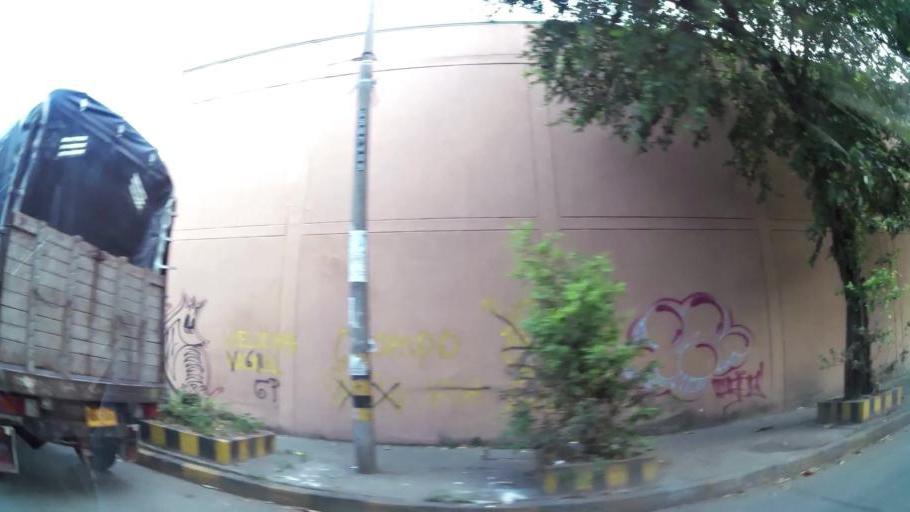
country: CO
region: Valle del Cauca
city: Cali
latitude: 3.4614
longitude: -76.5111
